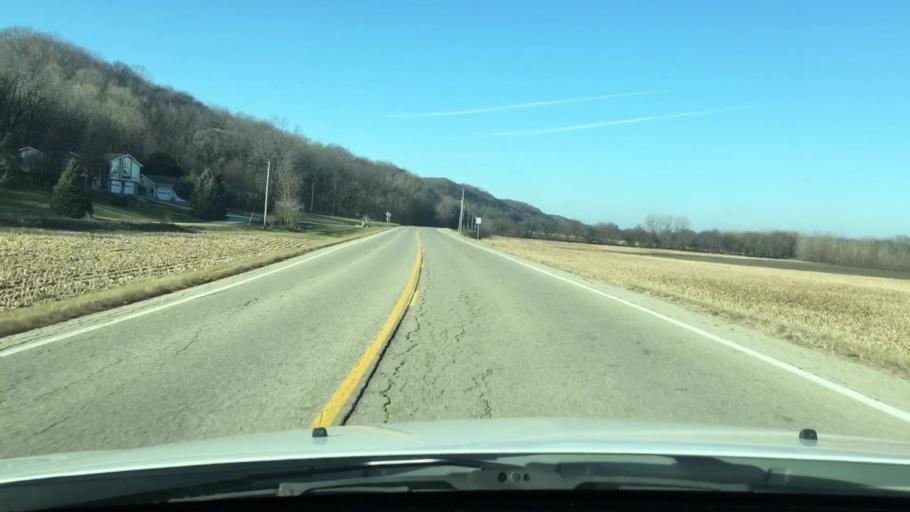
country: US
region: Illinois
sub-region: Bureau County
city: Spring Valley
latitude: 41.3002
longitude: -89.1673
